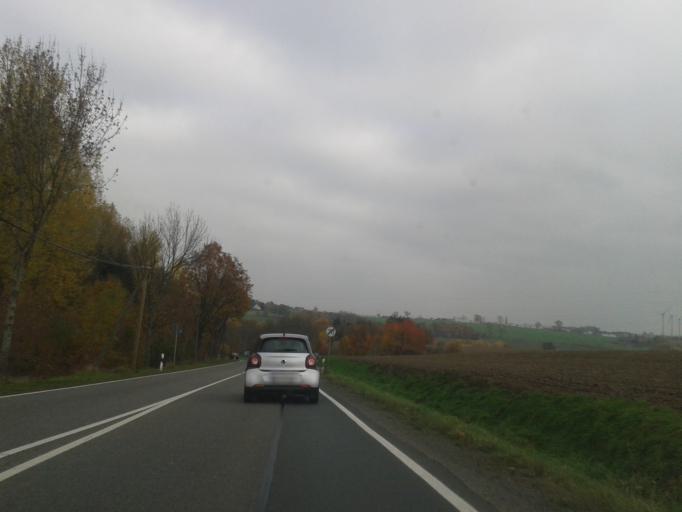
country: DE
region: Saxony
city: Freiberg
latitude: 50.9140
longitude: 13.3695
